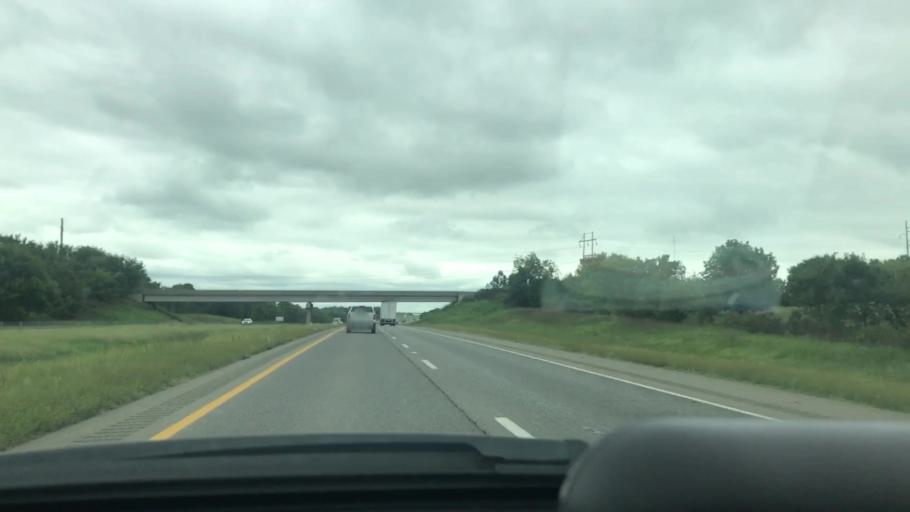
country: US
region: Oklahoma
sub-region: McIntosh County
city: Checotah
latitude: 35.3896
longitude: -95.5660
